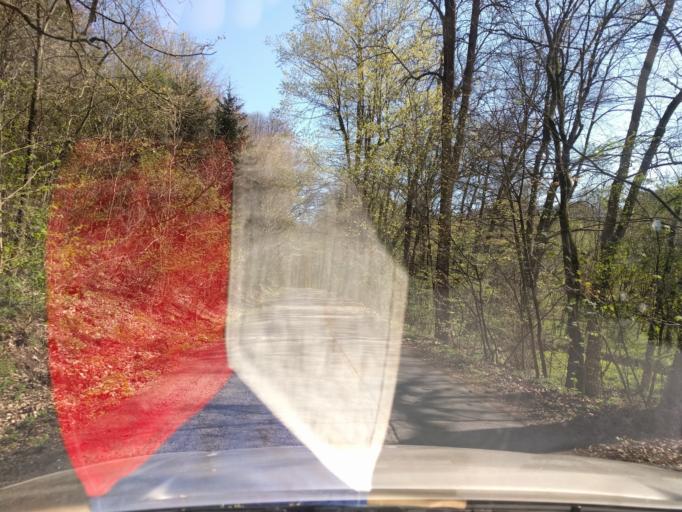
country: CZ
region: Central Bohemia
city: Cesky Brod
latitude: 50.0368
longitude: 14.8321
